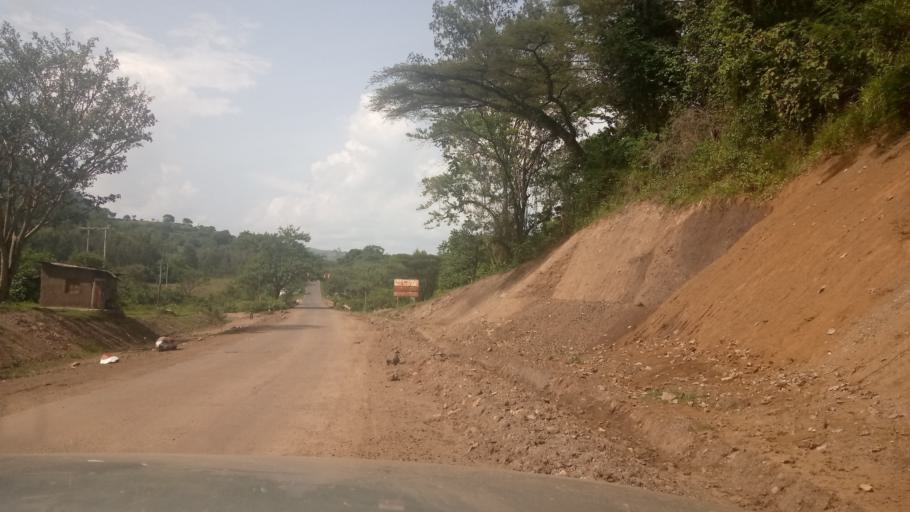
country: ET
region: Oromiya
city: Agaro
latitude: 8.0437
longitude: 36.4730
